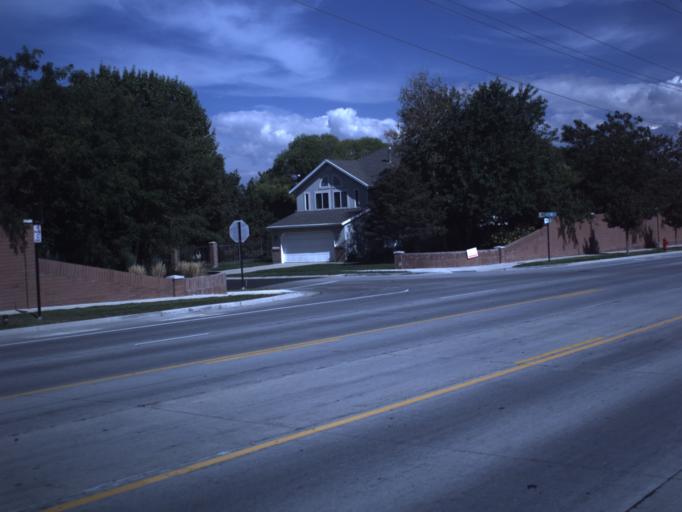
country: US
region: Utah
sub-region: Salt Lake County
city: South Jordan Heights
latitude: 40.5441
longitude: -111.9540
